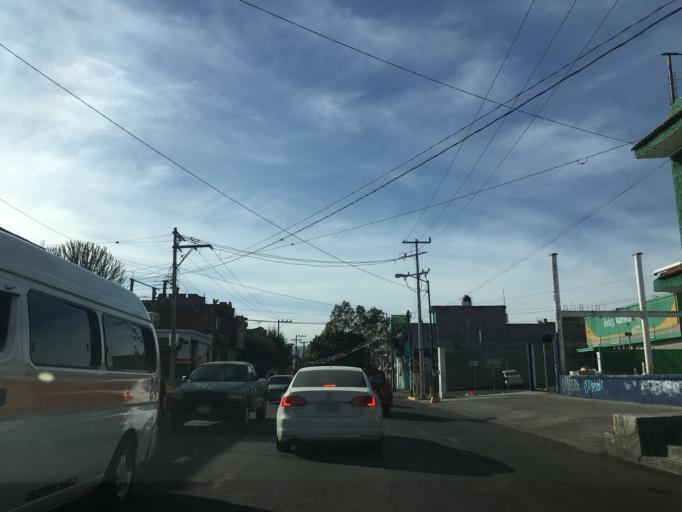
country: MX
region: Michoacan
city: Morelia
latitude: 19.7081
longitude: -101.2073
